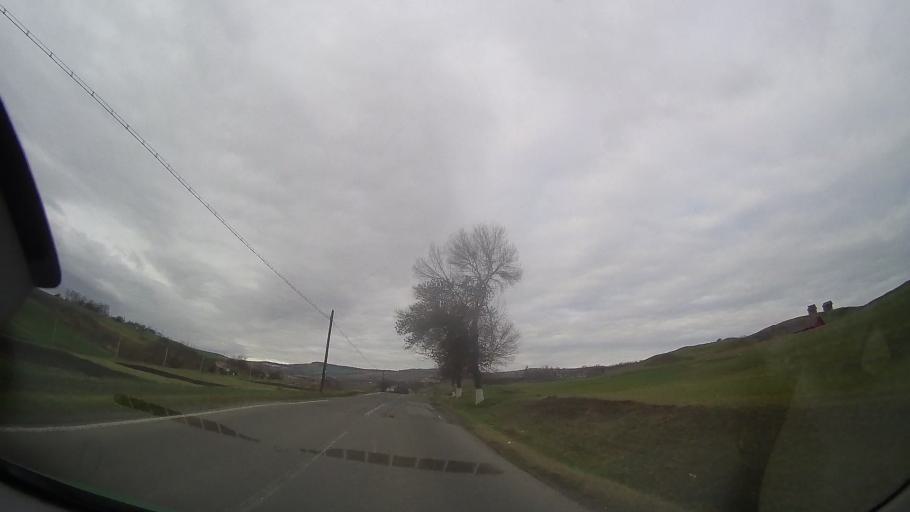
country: RO
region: Bistrita-Nasaud
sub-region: Comuna Urmenis
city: Urmenis
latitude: 46.7622
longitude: 24.3800
